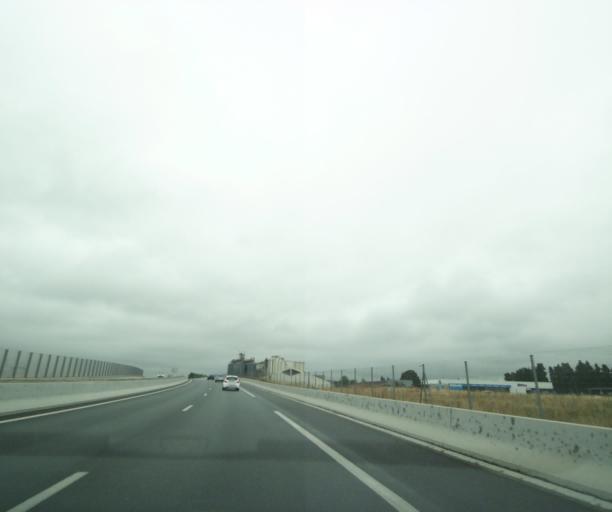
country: FR
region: Midi-Pyrenees
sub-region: Departement du Tarn
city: Puygouzon
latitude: 43.9172
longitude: 2.1645
